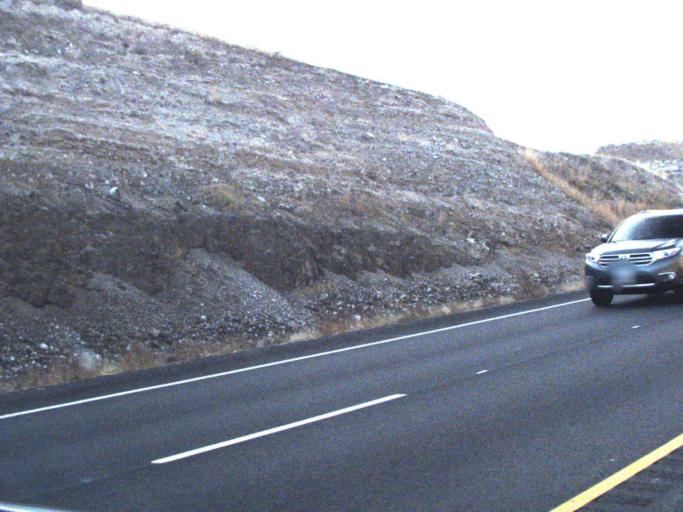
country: US
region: Washington
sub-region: Walla Walla County
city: Burbank
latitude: 46.0673
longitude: -118.7598
